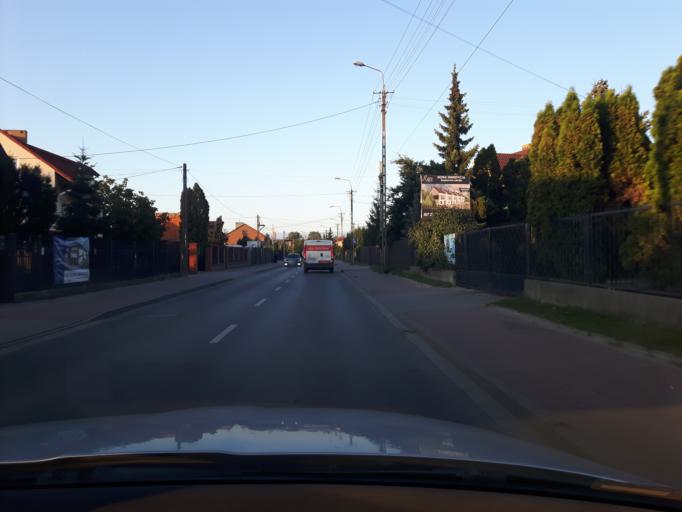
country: PL
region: Masovian Voivodeship
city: Zielonka
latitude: 52.3272
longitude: 21.1692
